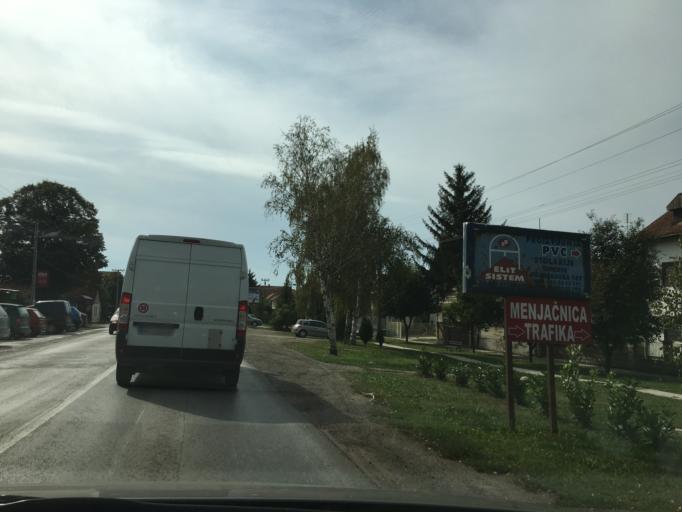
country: RS
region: Autonomna Pokrajina Vojvodina
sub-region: Juznobacki Okrug
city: Temerin
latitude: 45.3911
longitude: 19.8807
